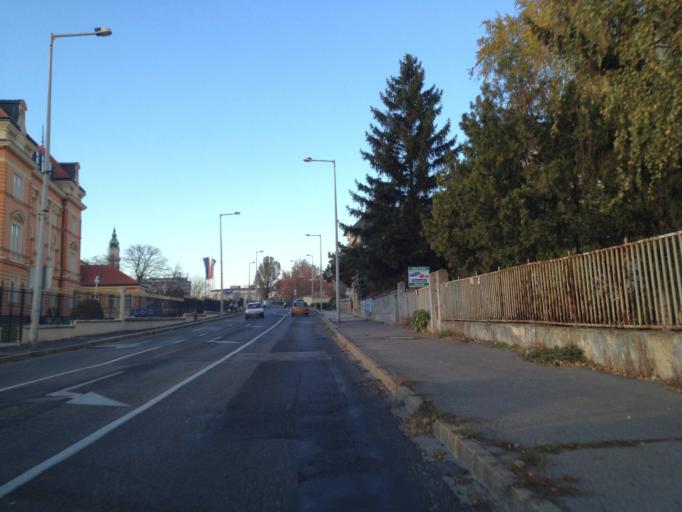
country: HU
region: Gyor-Moson-Sopron
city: Gyor
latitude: 47.6800
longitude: 17.6383
